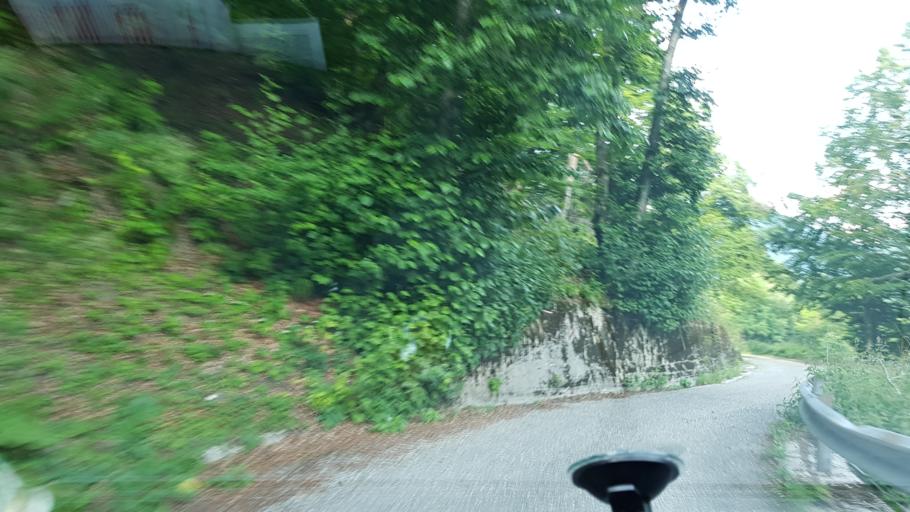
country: IT
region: Friuli Venezia Giulia
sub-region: Provincia di Udine
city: Prato
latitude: 46.3285
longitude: 13.3605
